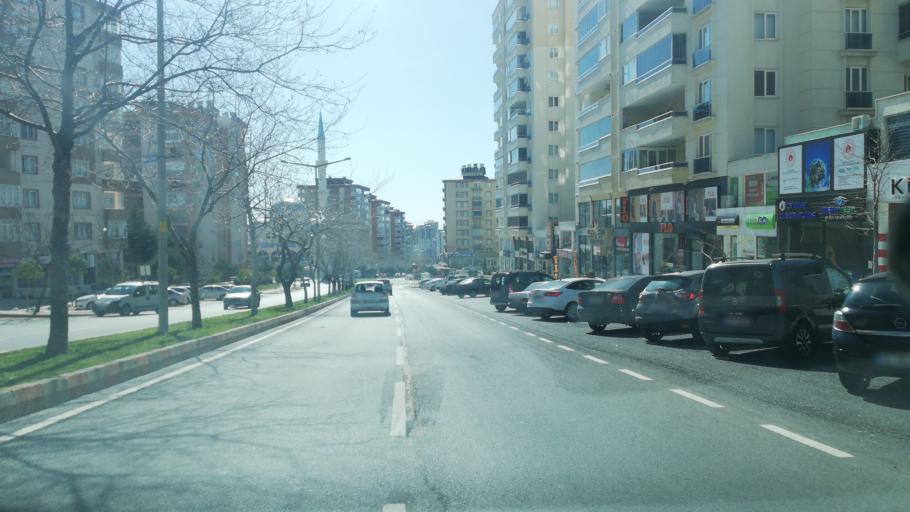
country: TR
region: Kahramanmaras
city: Kahramanmaras
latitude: 37.5883
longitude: 36.8781
